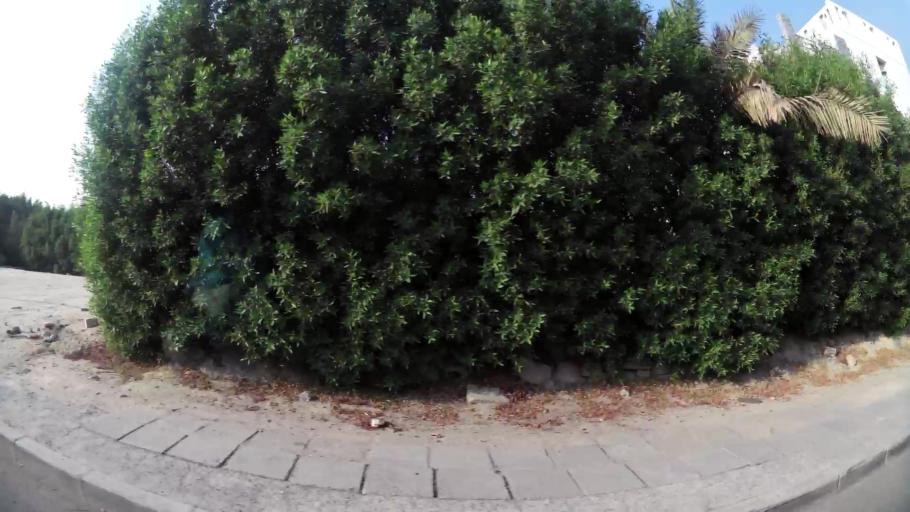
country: KW
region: Muhafazat Hawalli
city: Salwa
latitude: 29.2915
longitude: 48.0636
